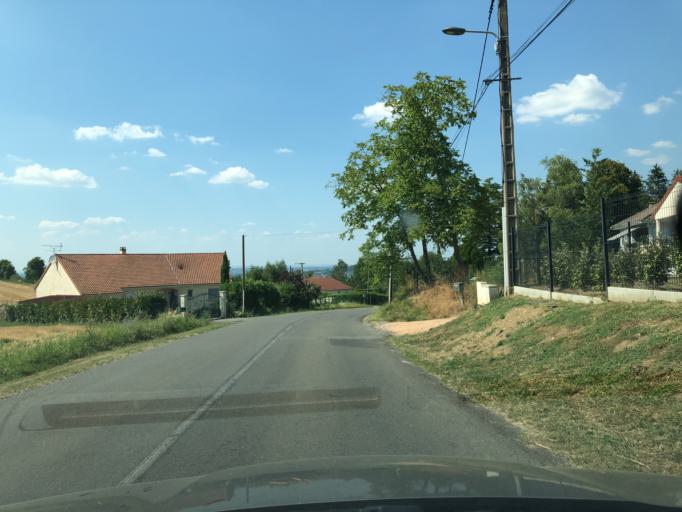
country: FR
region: Auvergne
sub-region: Departement de l'Allier
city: Cusset
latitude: 46.1132
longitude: 3.4624
